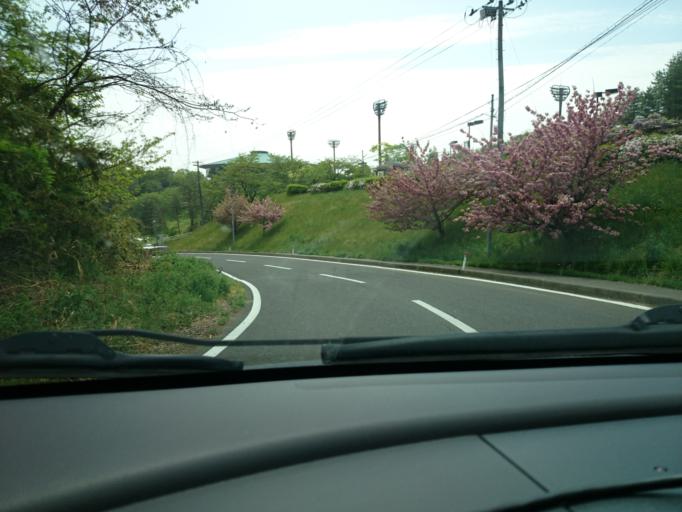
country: JP
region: Fukushima
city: Nihommatsu
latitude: 37.6038
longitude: 140.4302
